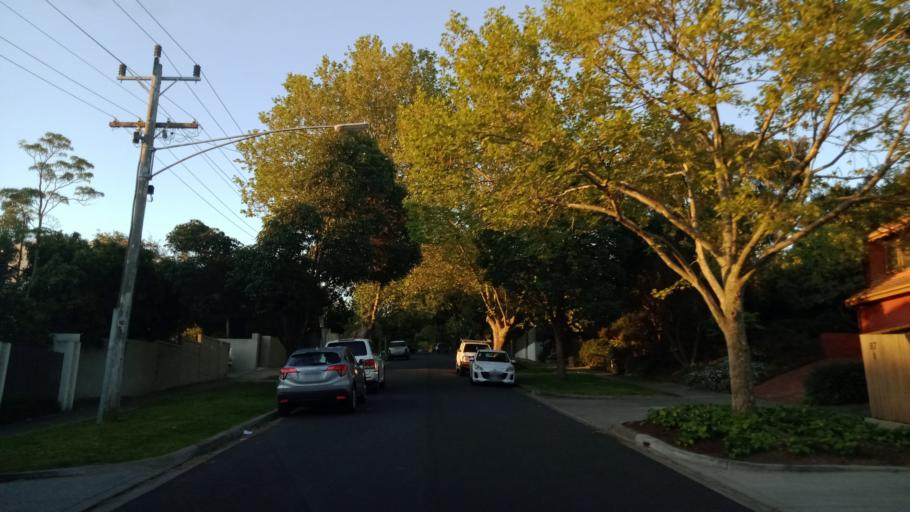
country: AU
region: Victoria
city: Glenferrie
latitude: -37.8357
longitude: 145.0360
